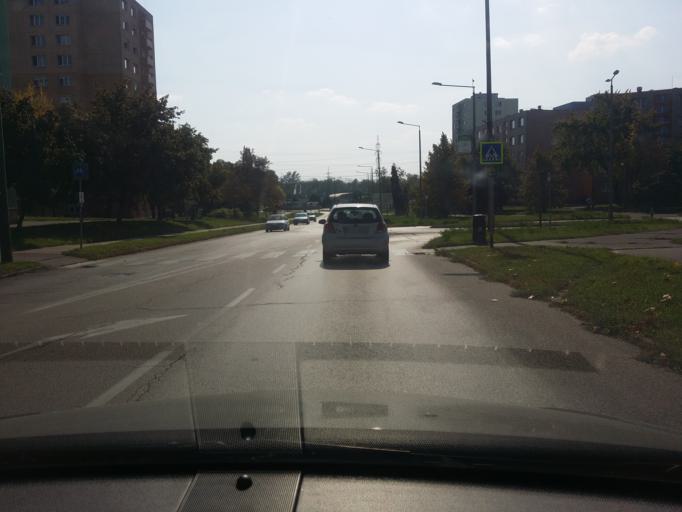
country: HU
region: Fejer
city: dunaujvaros
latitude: 46.9603
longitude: 18.9208
